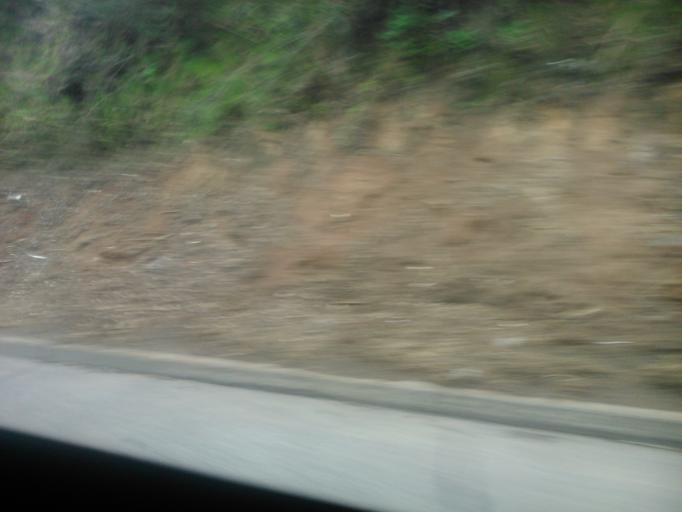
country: CL
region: Maule
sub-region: Provincia de Talca
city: Talca
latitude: -35.3506
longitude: -71.5754
